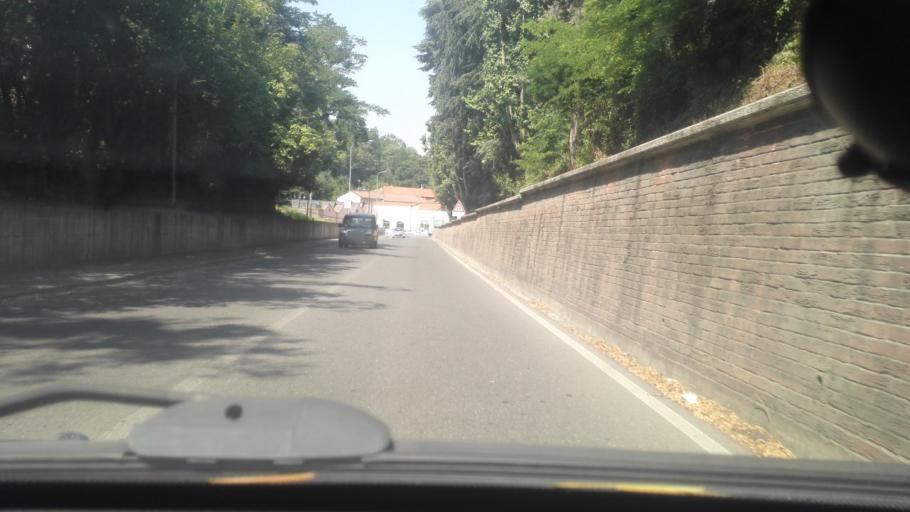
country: IT
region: Piedmont
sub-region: Provincia di Alessandria
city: Novi Ligure
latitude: 44.7570
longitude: 8.7877
